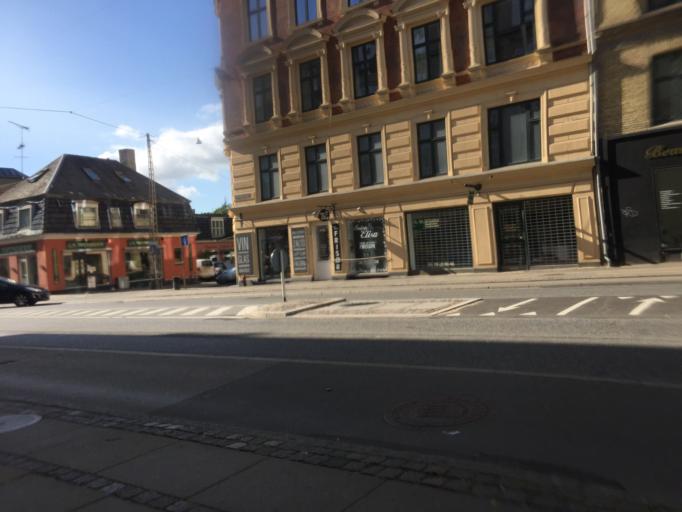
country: DK
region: Capital Region
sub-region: Frederiksberg Kommune
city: Frederiksberg
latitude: 55.6796
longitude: 12.5245
